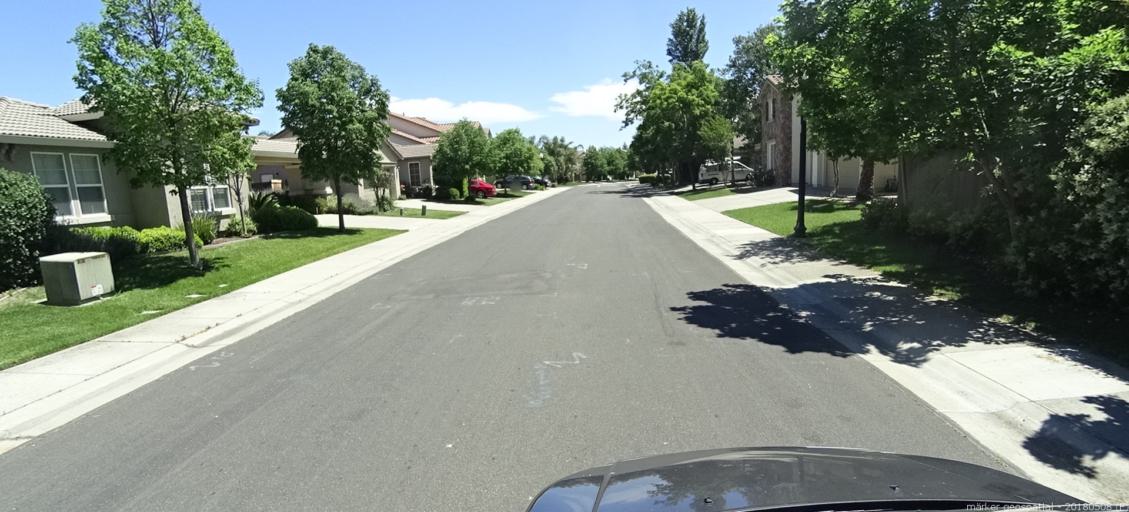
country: US
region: California
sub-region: Sacramento County
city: Elverta
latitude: 38.6780
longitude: -121.5237
